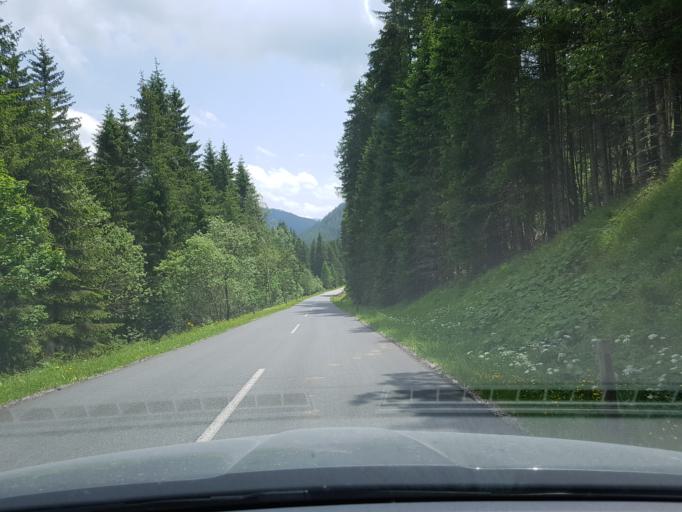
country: AT
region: Carinthia
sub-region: Politischer Bezirk Spittal an der Drau
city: Kleinkirchheim
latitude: 46.8786
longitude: 13.8581
